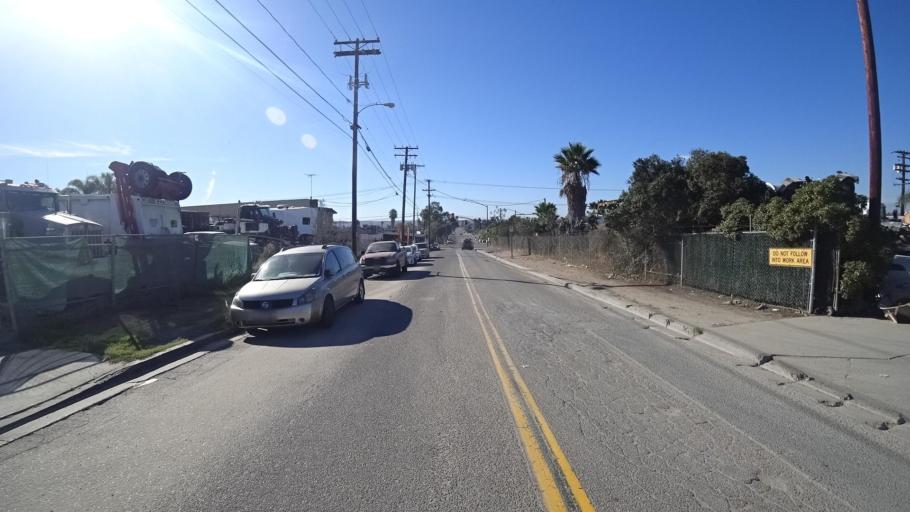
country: US
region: California
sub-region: San Diego County
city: La Presa
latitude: 32.7158
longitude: -116.9973
